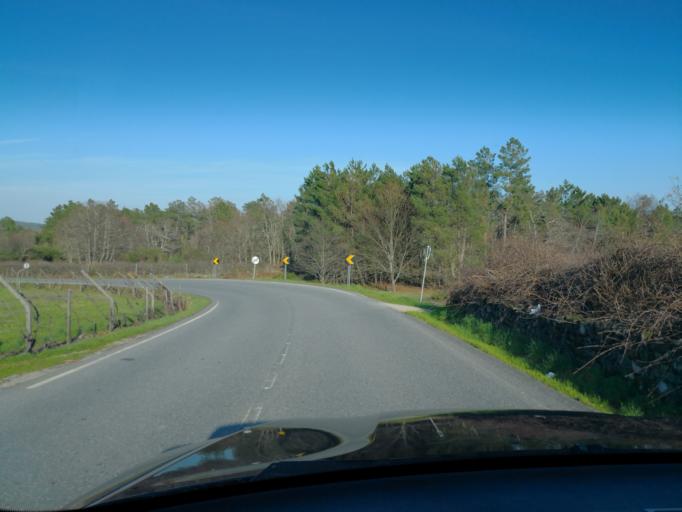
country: PT
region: Vila Real
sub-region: Sabrosa
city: Sabrosa
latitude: 41.3509
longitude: -7.6051
